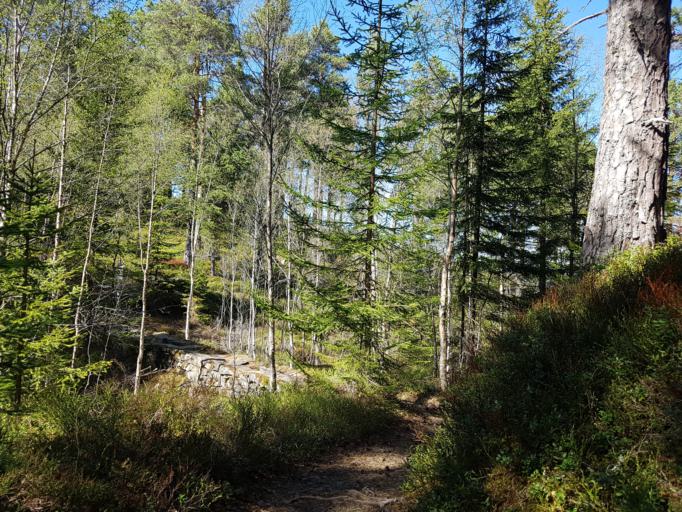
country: NO
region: Sor-Trondelag
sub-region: Trondheim
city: Trondheim
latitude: 63.4412
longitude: 10.3154
